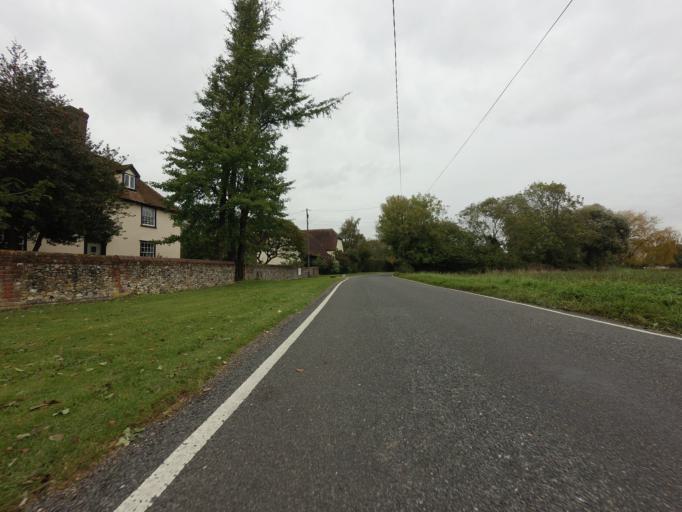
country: GB
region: England
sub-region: Cambridgeshire
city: Duxford
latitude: 52.0087
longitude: 0.1236
